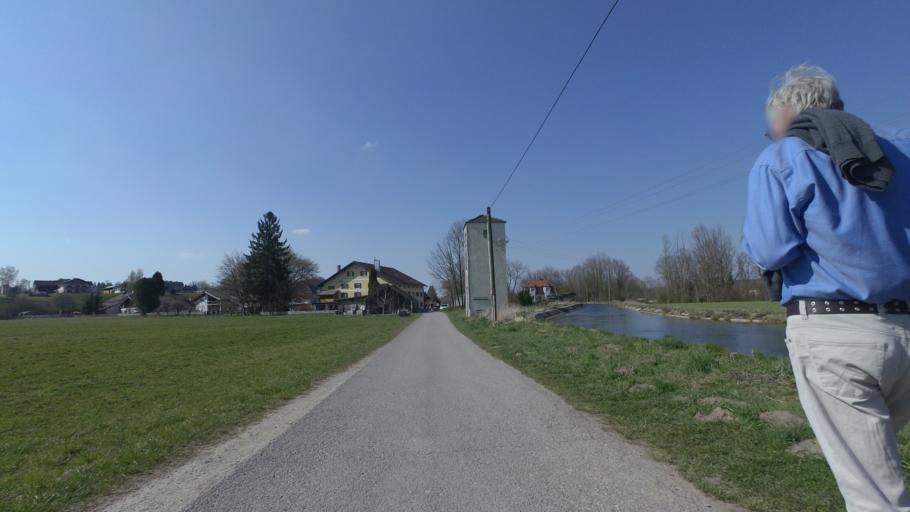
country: DE
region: Bavaria
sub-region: Upper Bavaria
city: Traunreut
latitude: 47.9599
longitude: 12.5720
